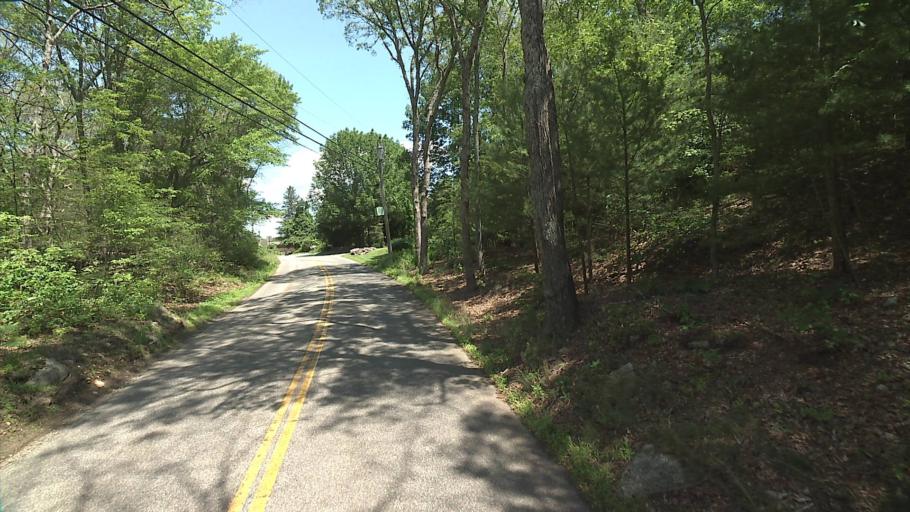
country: US
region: Connecticut
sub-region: New London County
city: Preston City
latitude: 41.5332
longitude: -71.8800
